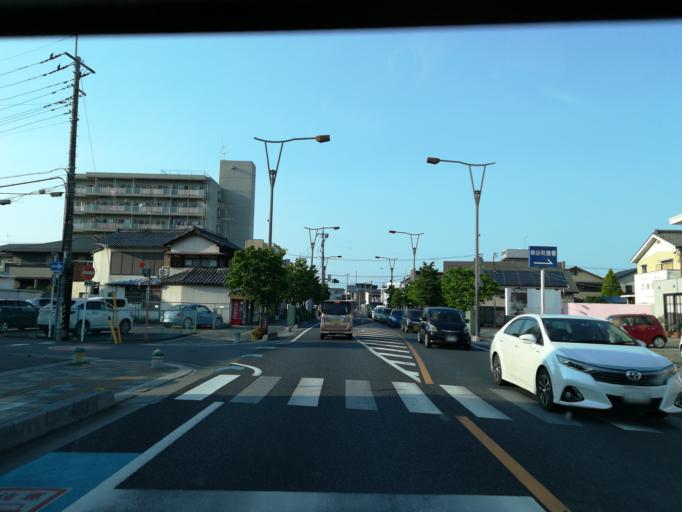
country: JP
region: Saitama
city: Kumagaya
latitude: 36.1475
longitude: 139.3821
